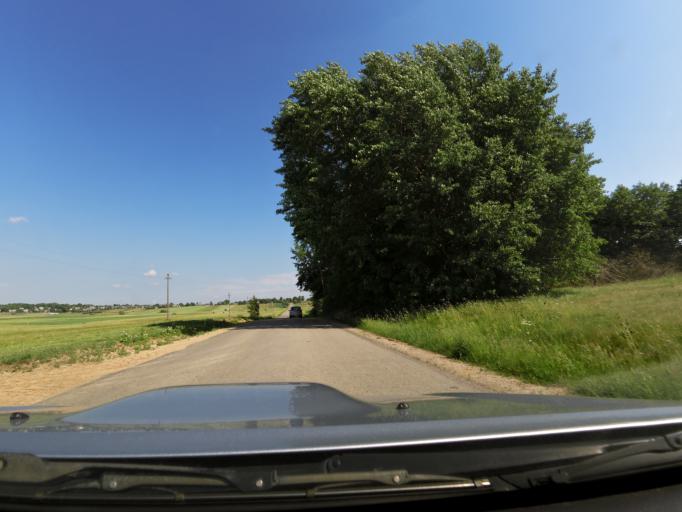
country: LT
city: Vilkaviskis
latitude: 54.5050
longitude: 23.0069
